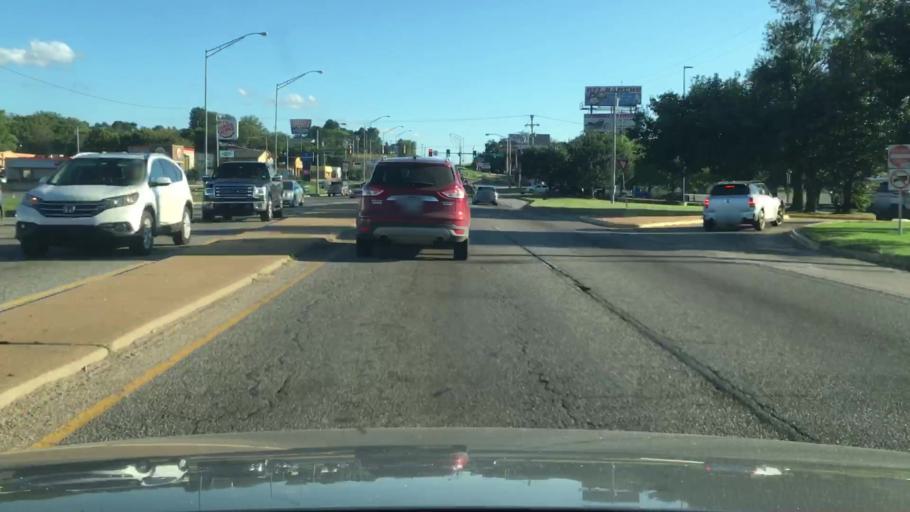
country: US
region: Oklahoma
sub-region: Cherokee County
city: Tahlequah
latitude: 35.8893
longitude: -94.9771
